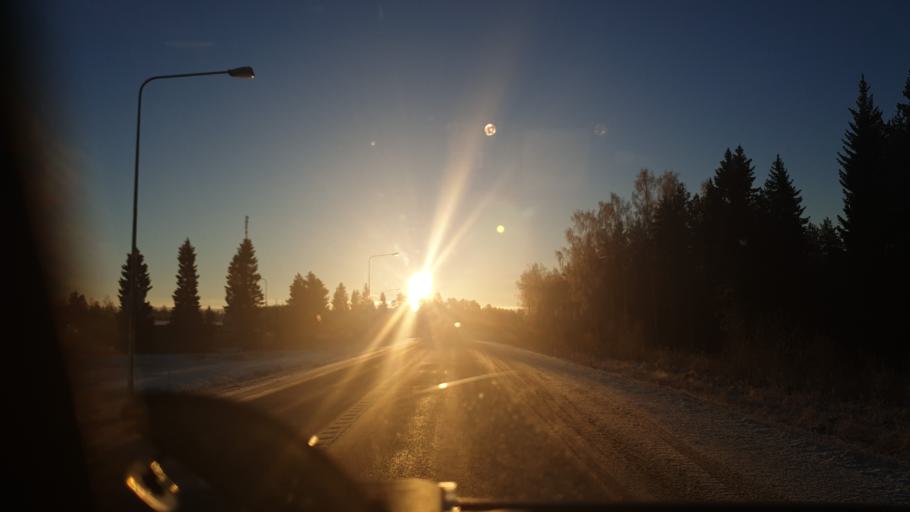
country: FI
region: Northern Ostrobothnia
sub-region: Ylivieska
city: Kalajoki
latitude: 64.2849
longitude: 23.9473
